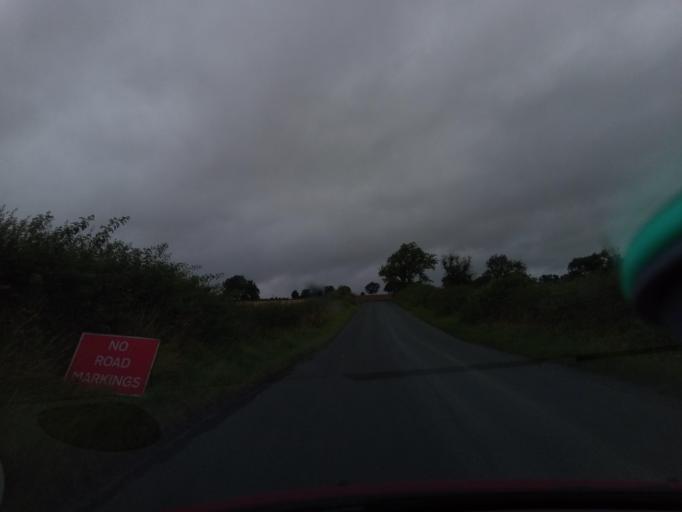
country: GB
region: Scotland
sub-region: The Scottish Borders
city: Kelso
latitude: 55.6142
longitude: -2.4657
